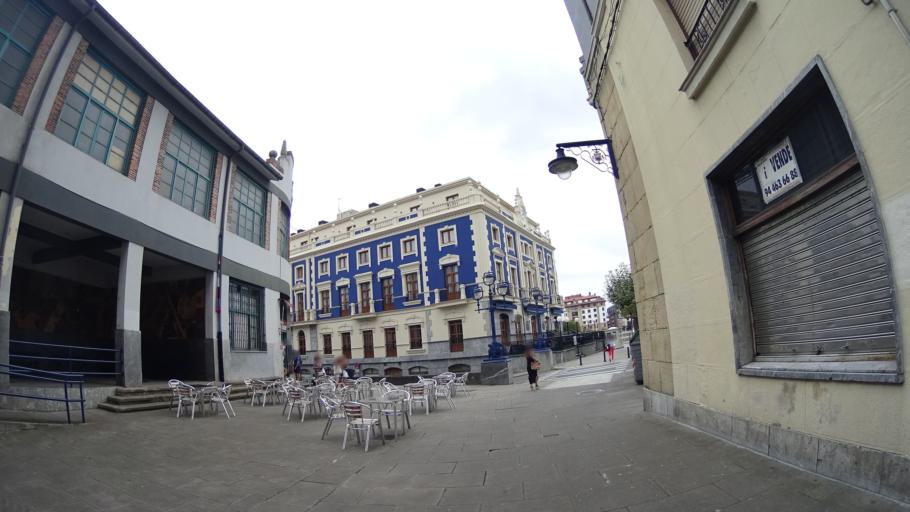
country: ES
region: Basque Country
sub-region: Bizkaia
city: Portugalete
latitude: 43.3216
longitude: -3.0177
